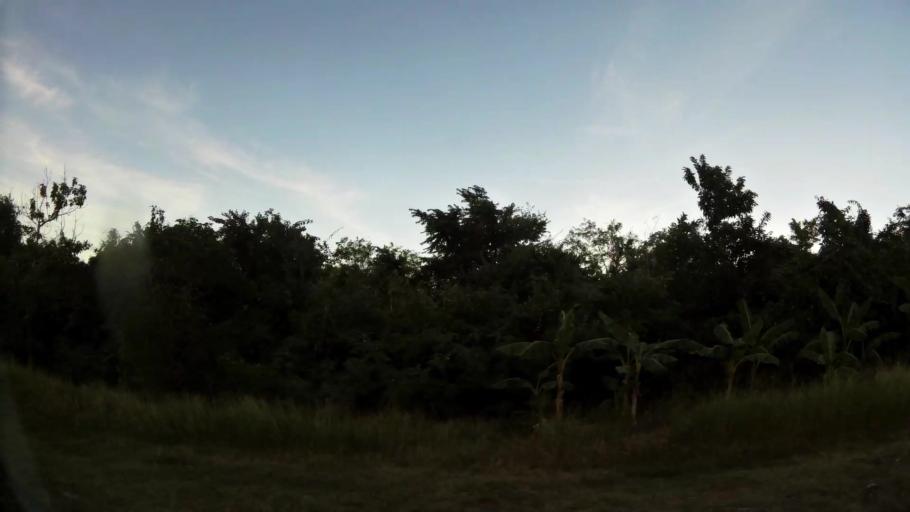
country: LC
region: Gros-Islet
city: Gros Islet
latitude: 14.0758
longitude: -60.9427
